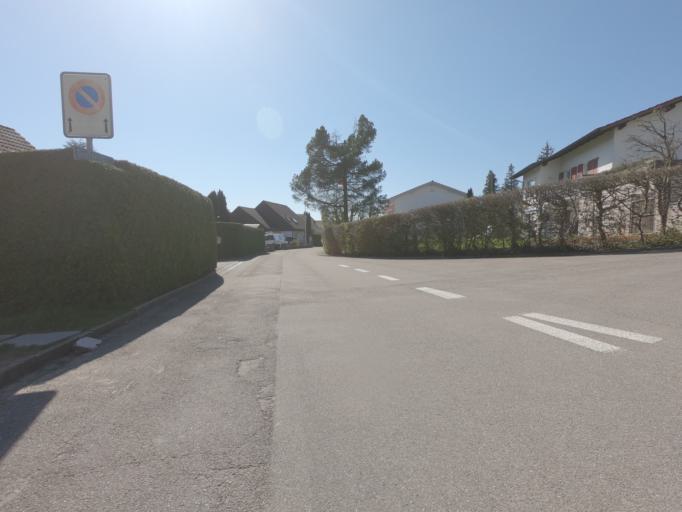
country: CH
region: Solothurn
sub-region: Bezirk Lebern
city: Riedholz
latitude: 47.2321
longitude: 7.5726
